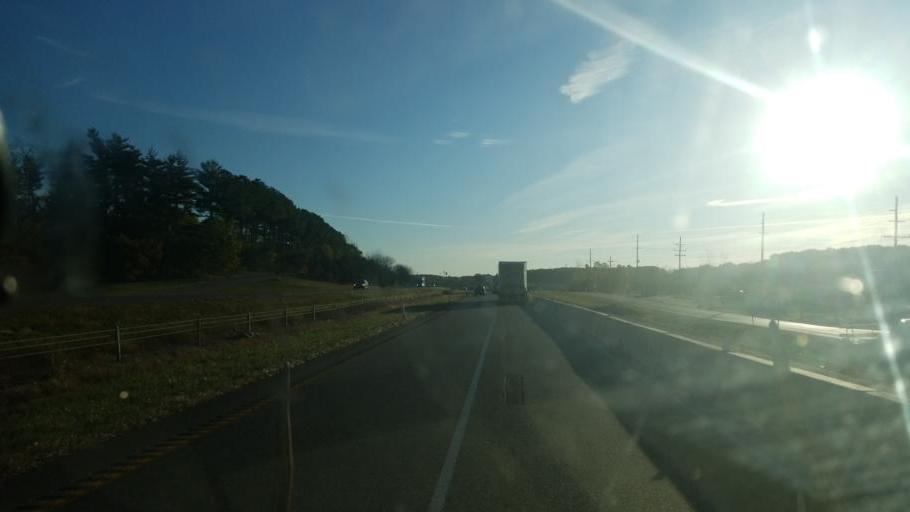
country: US
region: Missouri
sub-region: Warren County
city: Warrenton
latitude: 38.8196
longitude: -91.1716
